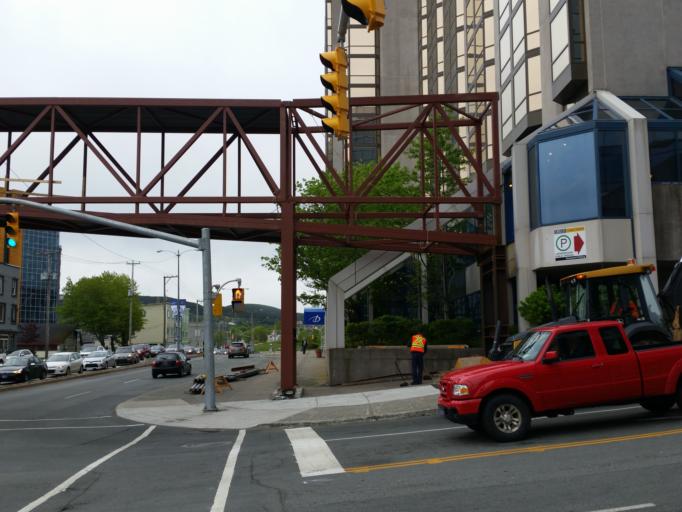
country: CA
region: Newfoundland and Labrador
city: St. John's
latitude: 47.5592
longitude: -52.7136
